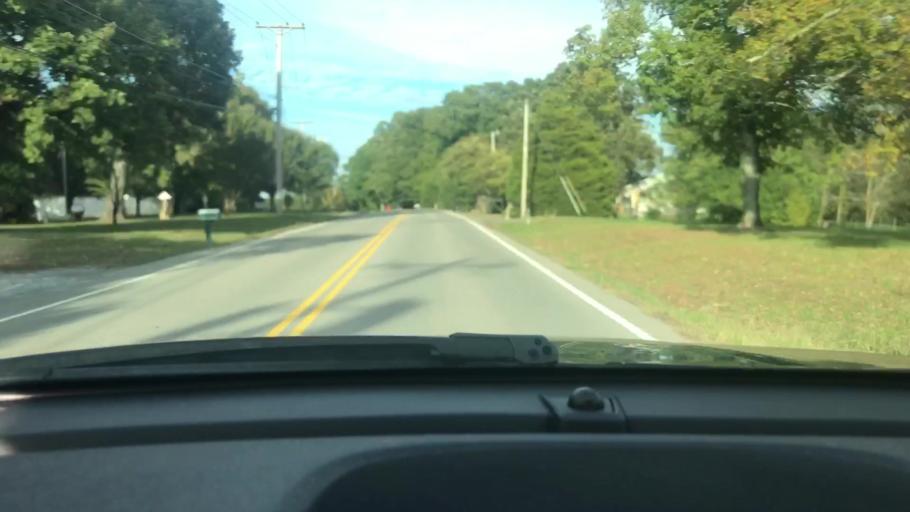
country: US
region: Tennessee
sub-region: Dickson County
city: White Bluff
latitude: 36.1397
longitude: -87.2378
